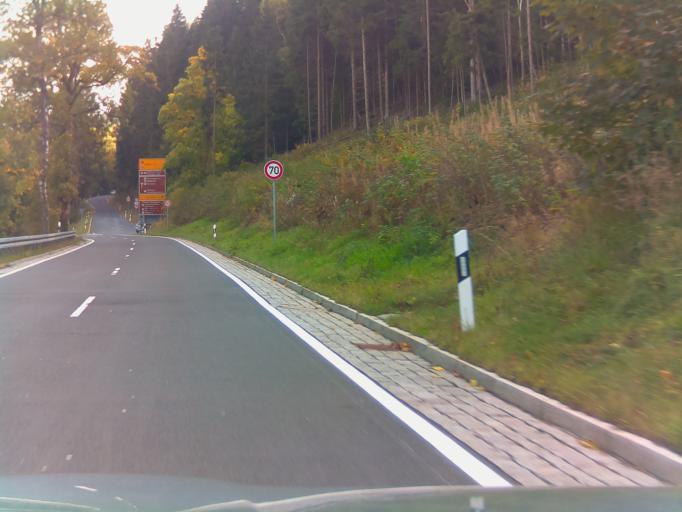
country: DE
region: Thuringia
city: Bermbach
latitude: 50.6967
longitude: 10.6303
